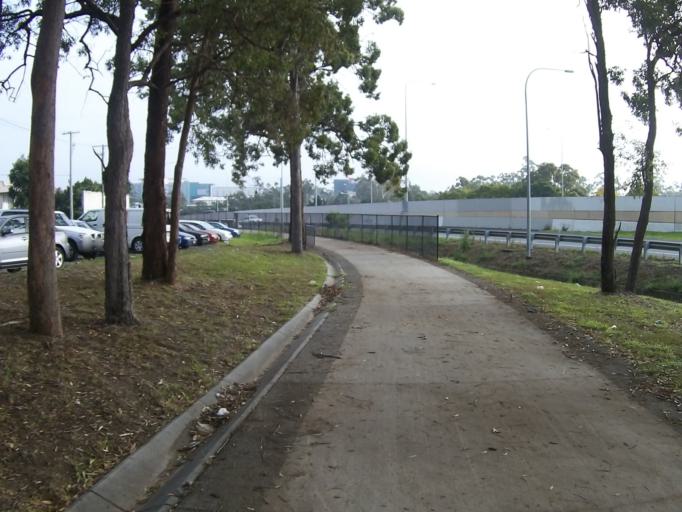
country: AU
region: Queensland
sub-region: Brisbane
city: Upper Mount Gravatt
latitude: -27.5702
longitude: 153.0893
